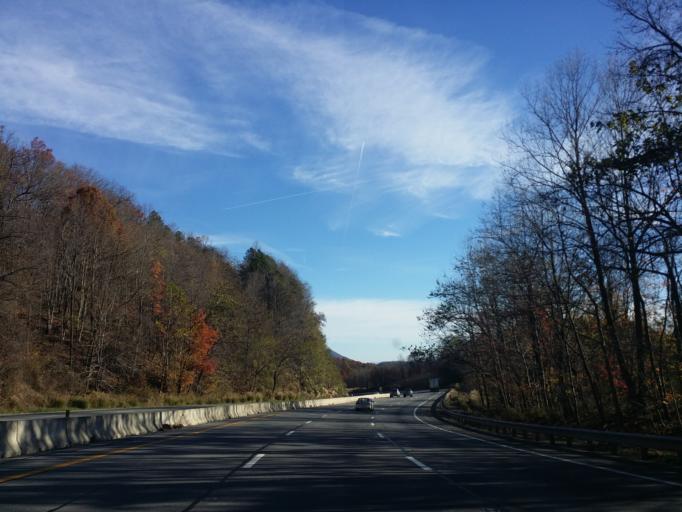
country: US
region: North Carolina
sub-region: Buncombe County
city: Black Mountain
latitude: 35.6173
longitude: -82.2432
